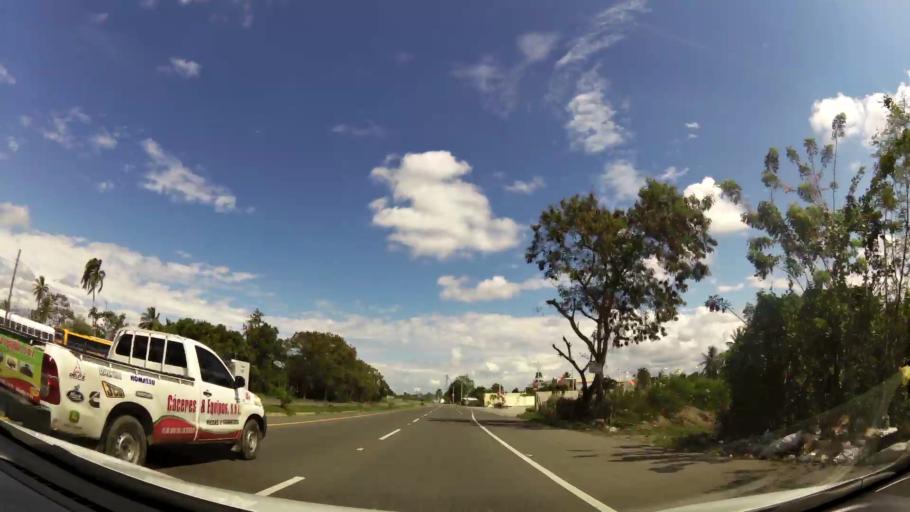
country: DO
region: La Vega
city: Concepcion de La Vega
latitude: 19.2469
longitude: -70.5451
